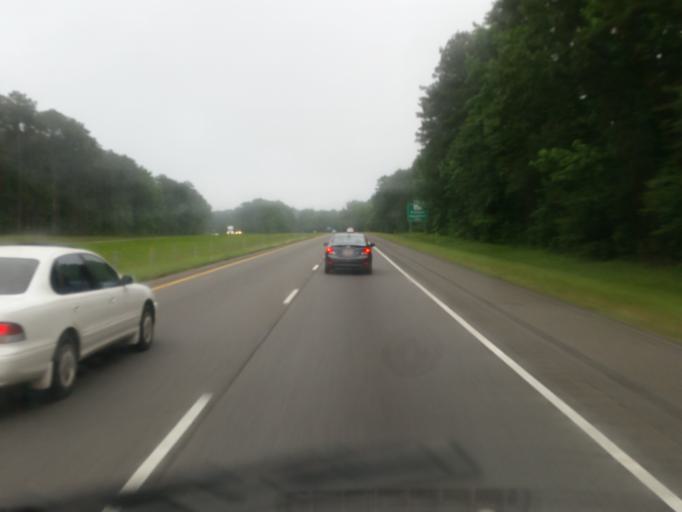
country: US
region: Louisiana
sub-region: Bossier Parish
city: Haughton
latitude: 32.5417
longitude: -93.5365
